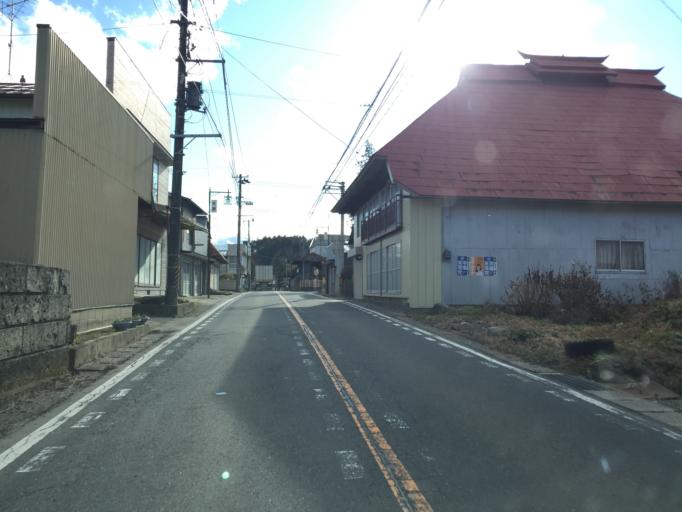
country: JP
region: Fukushima
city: Funehikimachi-funehiki
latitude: 37.4869
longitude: 140.5746
